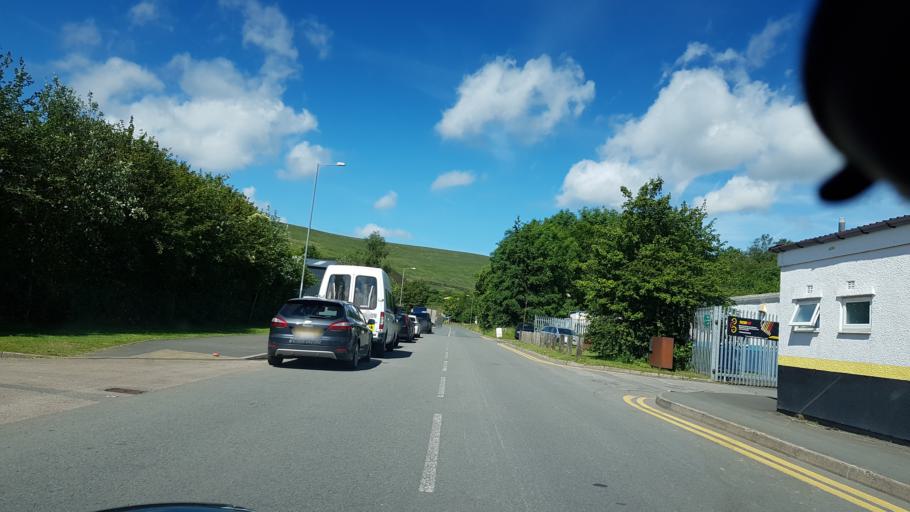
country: GB
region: Wales
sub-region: Torfaen County Borough
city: Blaenavon
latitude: 51.7757
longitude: -3.0975
